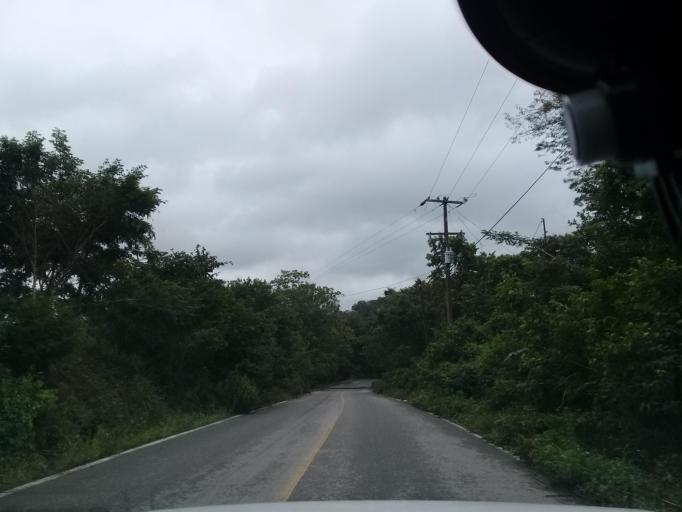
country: MX
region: Veracruz
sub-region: Chalma
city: San Pedro Coyutla
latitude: 21.2085
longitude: -98.4074
